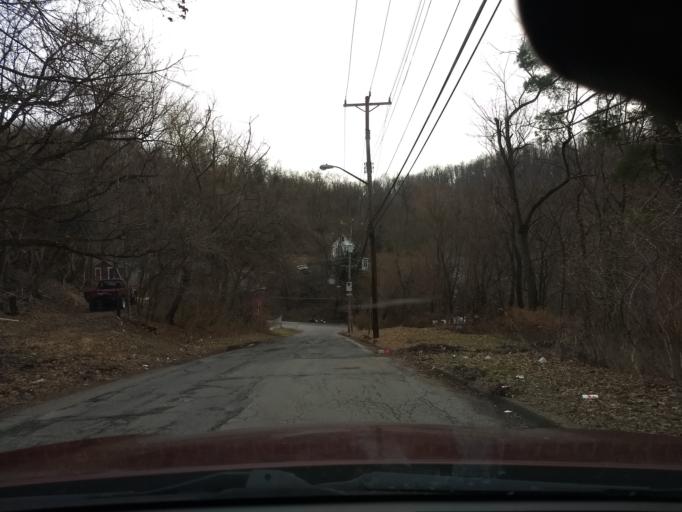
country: US
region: Pennsylvania
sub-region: Allegheny County
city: Homestead
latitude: 40.4127
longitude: -79.9370
